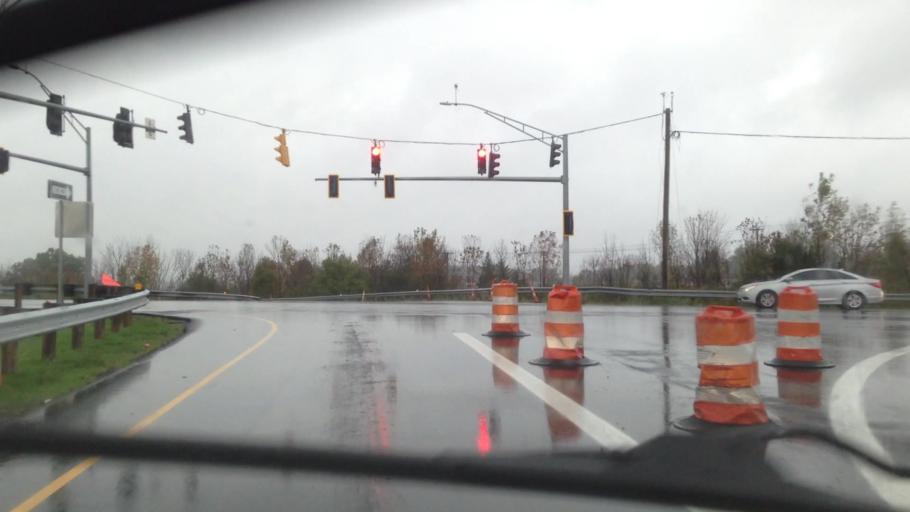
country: US
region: Ohio
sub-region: Portage County
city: Streetsboro
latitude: 41.2614
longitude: -81.3760
